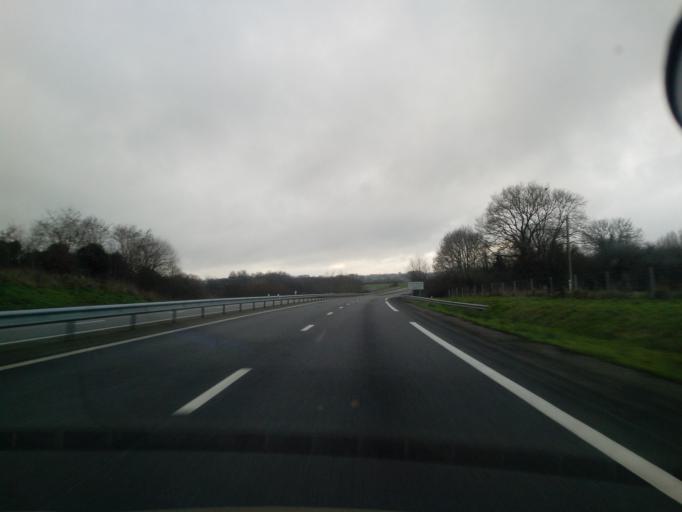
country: FR
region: Brittany
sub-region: Departement des Cotes-d'Armor
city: Plumaugat
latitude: 48.1906
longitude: -2.3109
